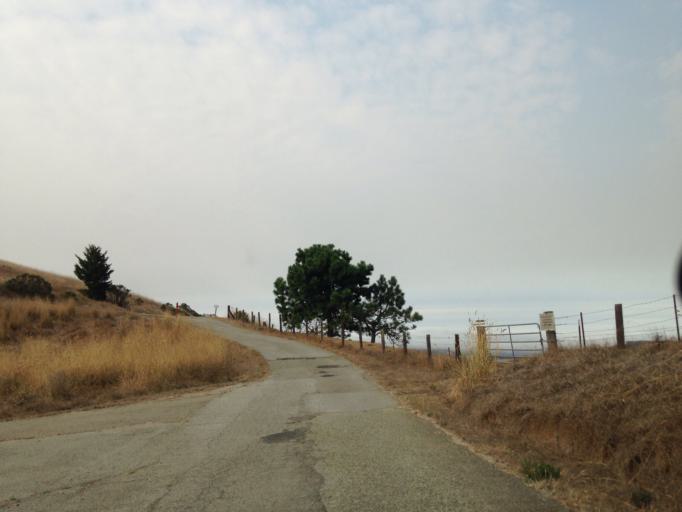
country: US
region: California
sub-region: San Mateo County
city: Portola Valley
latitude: 37.3710
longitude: -122.2984
